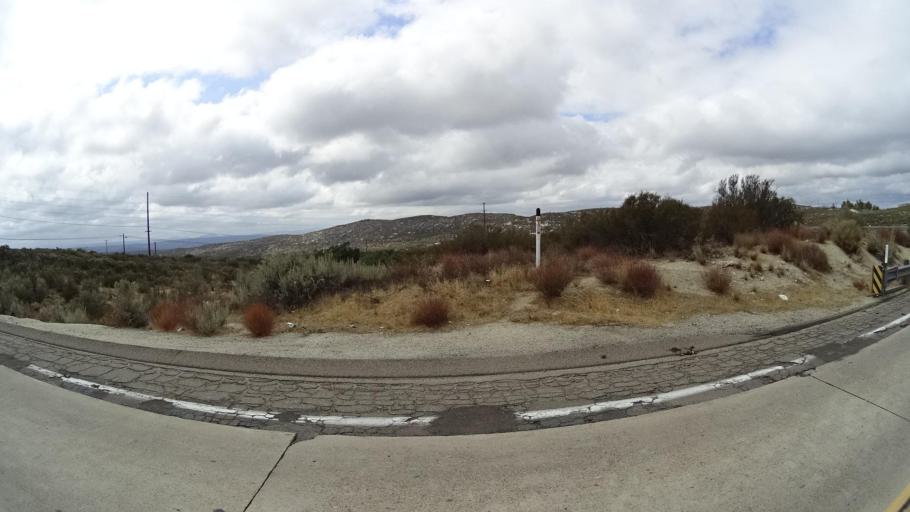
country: US
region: California
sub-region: San Diego County
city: Campo
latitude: 32.7004
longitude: -116.3568
